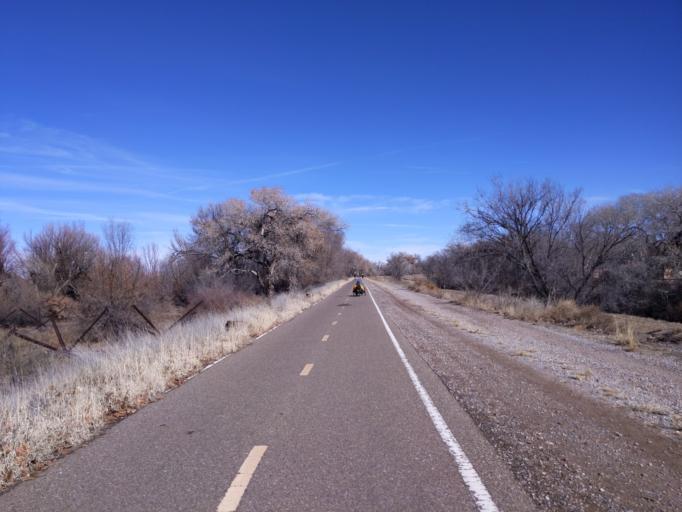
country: US
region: New Mexico
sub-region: Bernalillo County
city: Lee Acres
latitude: 35.1579
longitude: -106.6674
